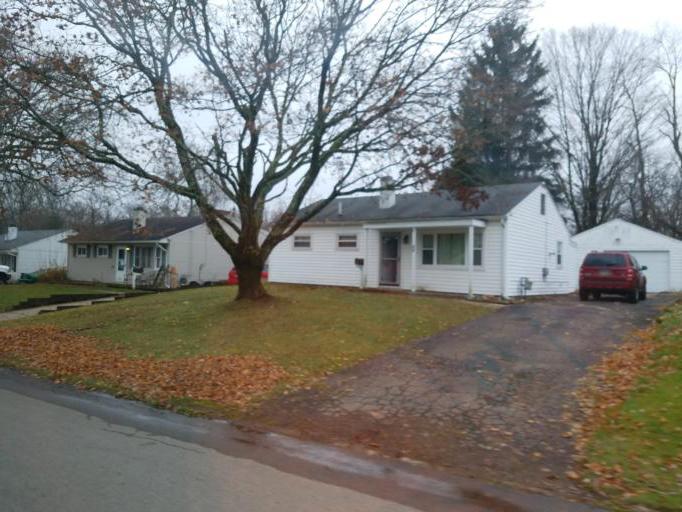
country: US
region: Ohio
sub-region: Richland County
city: Mansfield
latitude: 40.7354
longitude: -82.5118
